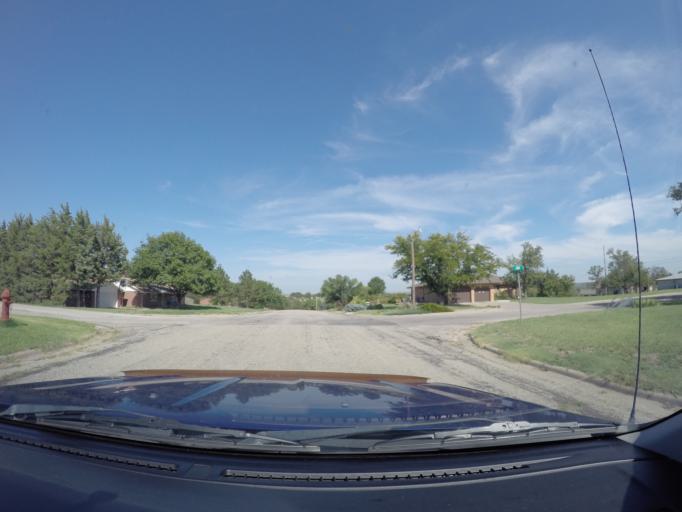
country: US
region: Kansas
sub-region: Rooks County
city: Stockton
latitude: 39.4423
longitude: -99.2709
